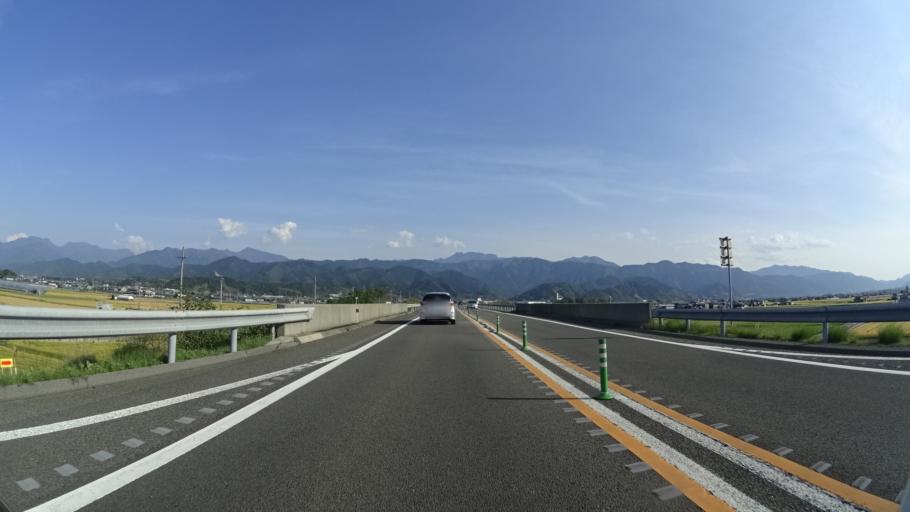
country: JP
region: Ehime
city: Saijo
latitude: 33.9058
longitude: 133.0747
